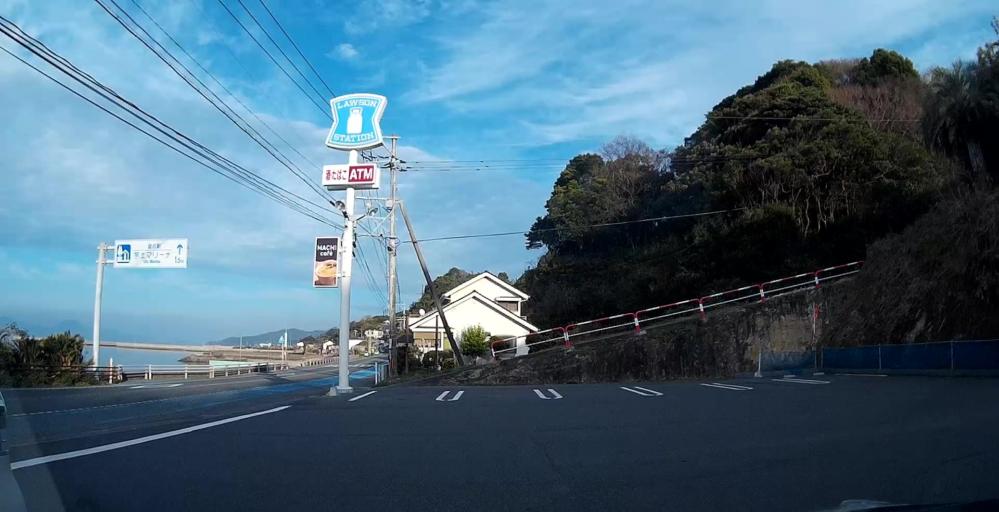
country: JP
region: Kumamoto
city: Matsubase
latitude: 32.6545
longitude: 130.5079
